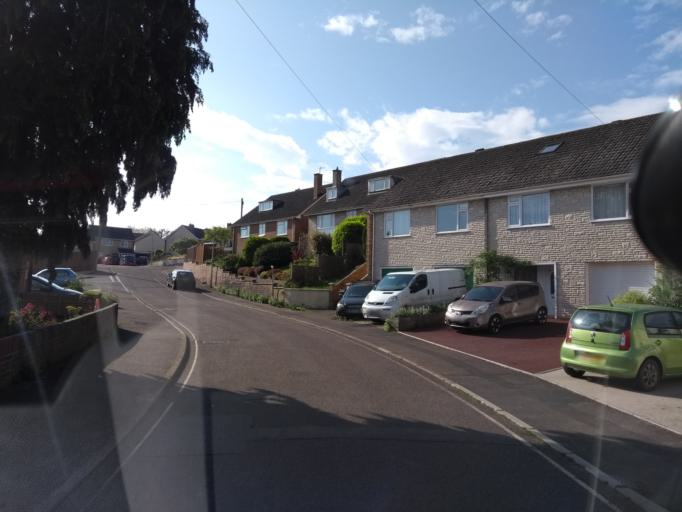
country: GB
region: England
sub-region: Devon
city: Axminster
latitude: 50.7804
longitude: -3.0021
